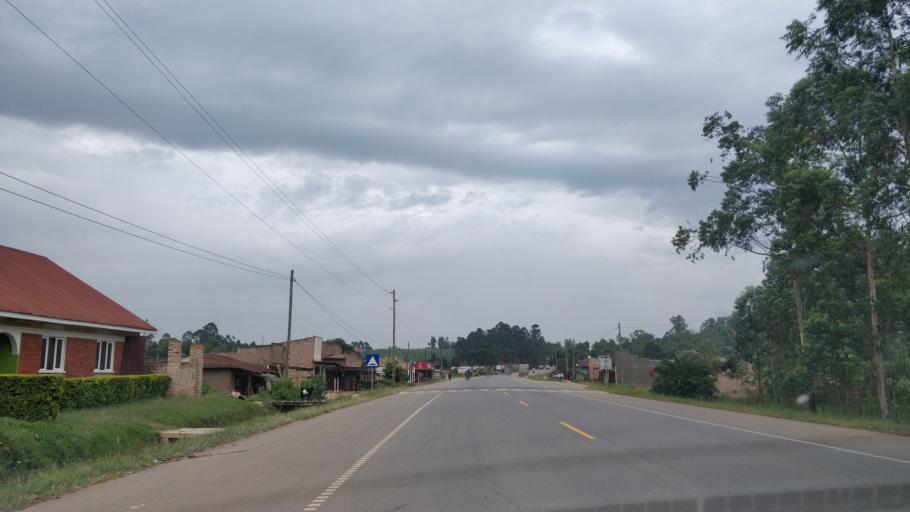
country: UG
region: Western Region
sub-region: Sheema District
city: Kibingo
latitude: -0.6599
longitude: 30.4578
